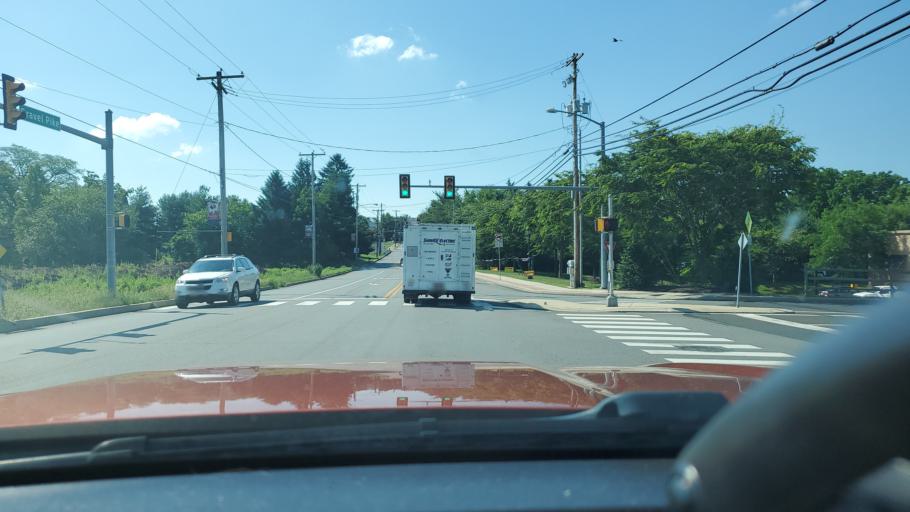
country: US
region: Pennsylvania
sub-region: Montgomery County
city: East Greenville
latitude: 40.4125
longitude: -75.5076
